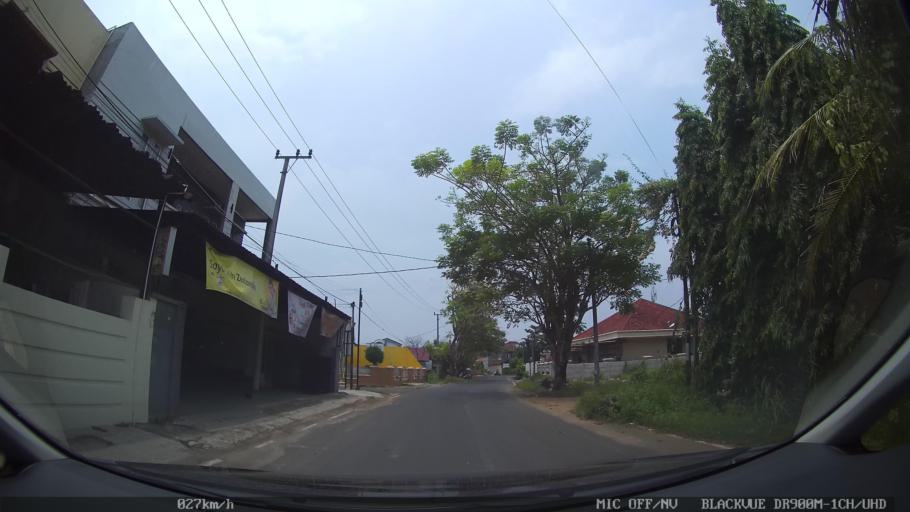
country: ID
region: Lampung
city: Bandarlampung
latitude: -5.4143
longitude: 105.2727
